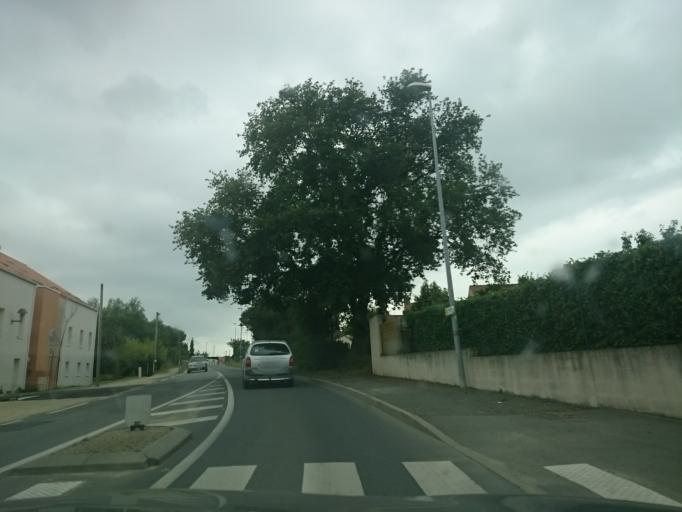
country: FR
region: Pays de la Loire
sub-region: Departement de la Loire-Atlantique
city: Saint-Jean-de-Boiseau
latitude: 47.1909
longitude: -1.7047
